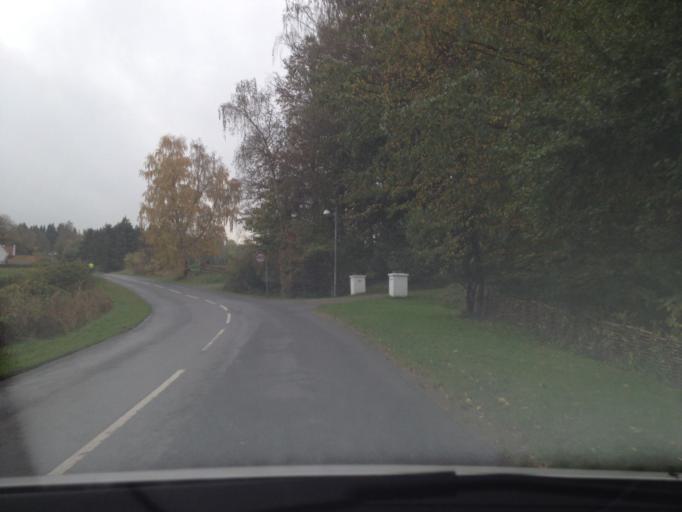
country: DK
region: Capital Region
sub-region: Hillerod Kommune
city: Nodebo
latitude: 55.9675
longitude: 12.3707
